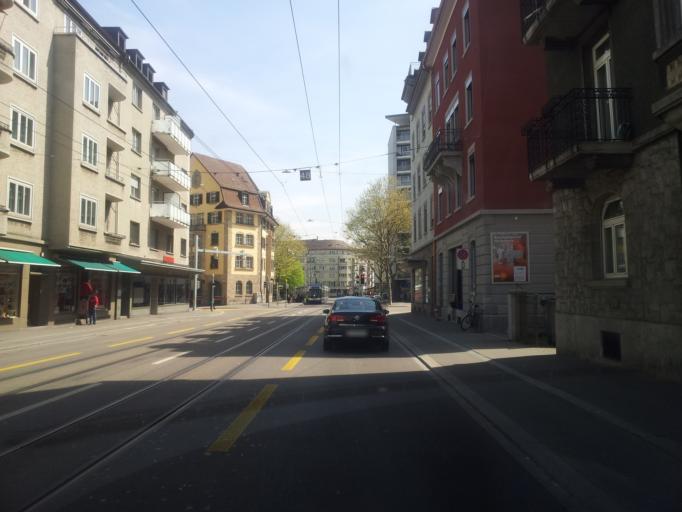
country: CH
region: Zurich
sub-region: Bezirk Zuerich
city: Zuerich (Kreis 3) / Sihlfeld
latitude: 47.3705
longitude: 8.5176
